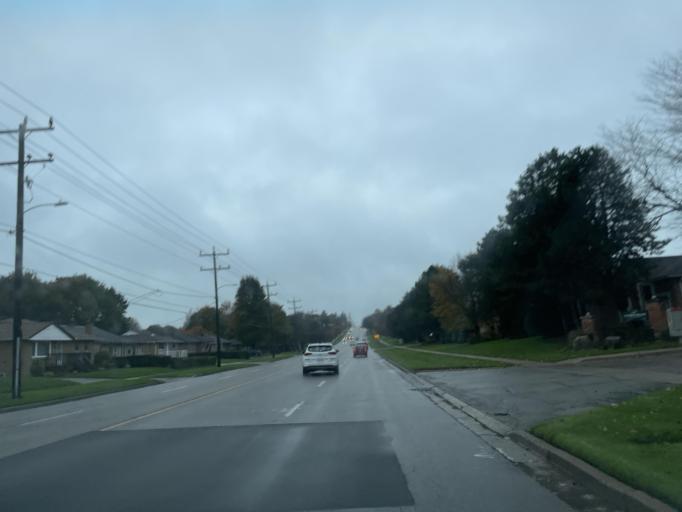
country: CA
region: Ontario
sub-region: Wellington County
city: Guelph
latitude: 43.5618
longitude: -80.2375
